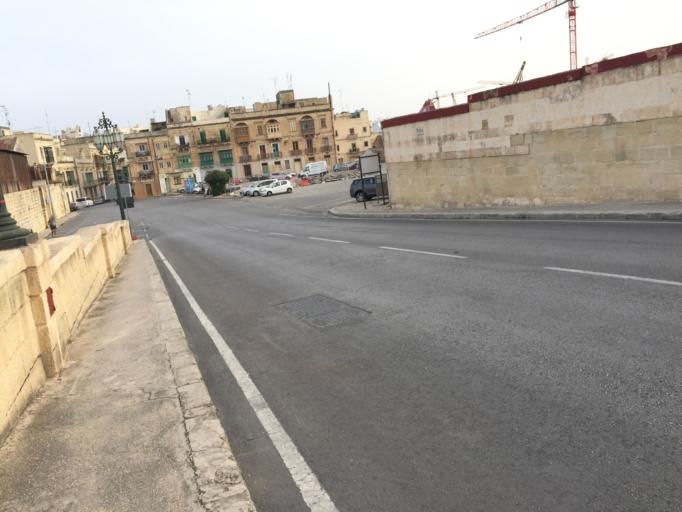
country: MT
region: L-Isla
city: Senglea
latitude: 35.8841
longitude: 14.5193
